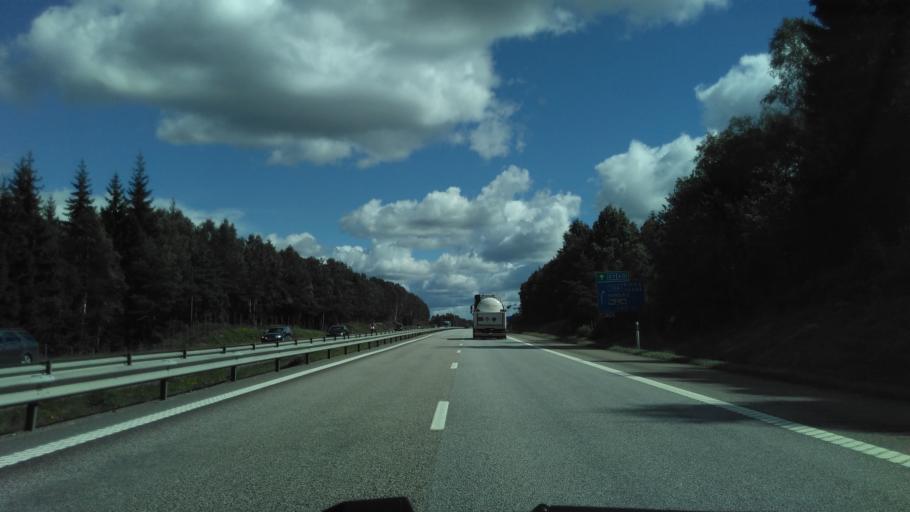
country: SE
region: Vaestra Goetaland
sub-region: Harryda Kommun
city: Hindas
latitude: 57.6774
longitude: 12.3385
